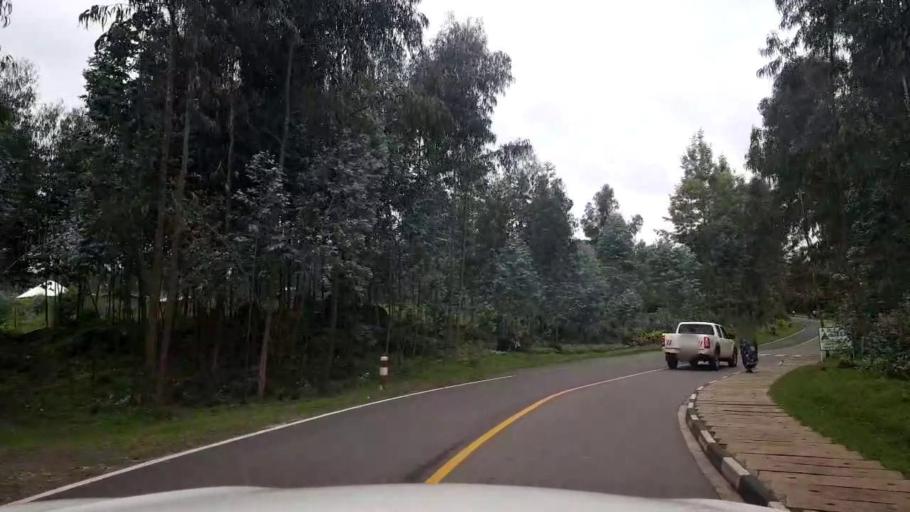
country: RW
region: Northern Province
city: Musanze
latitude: -1.4530
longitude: 29.6061
